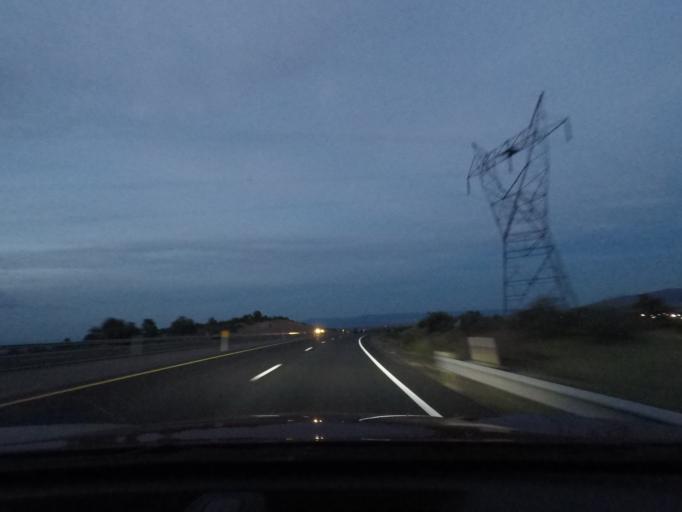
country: US
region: Arizona
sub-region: Yavapai County
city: Prescott
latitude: 34.6161
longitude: -112.4723
